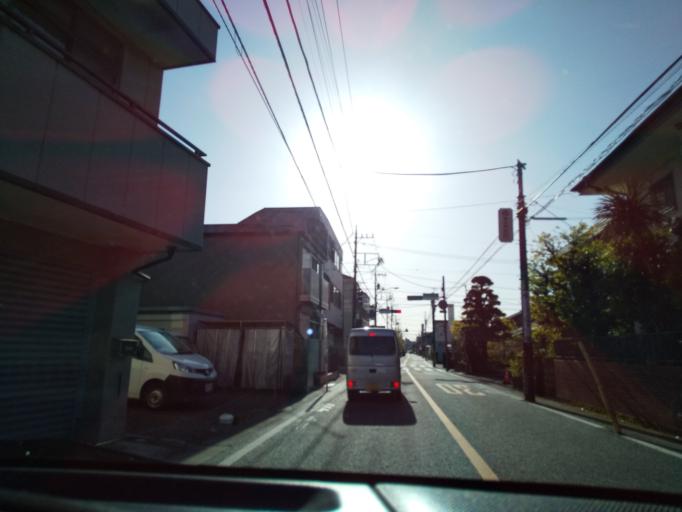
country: JP
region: Tokyo
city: Hino
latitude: 35.6927
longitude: 139.4037
